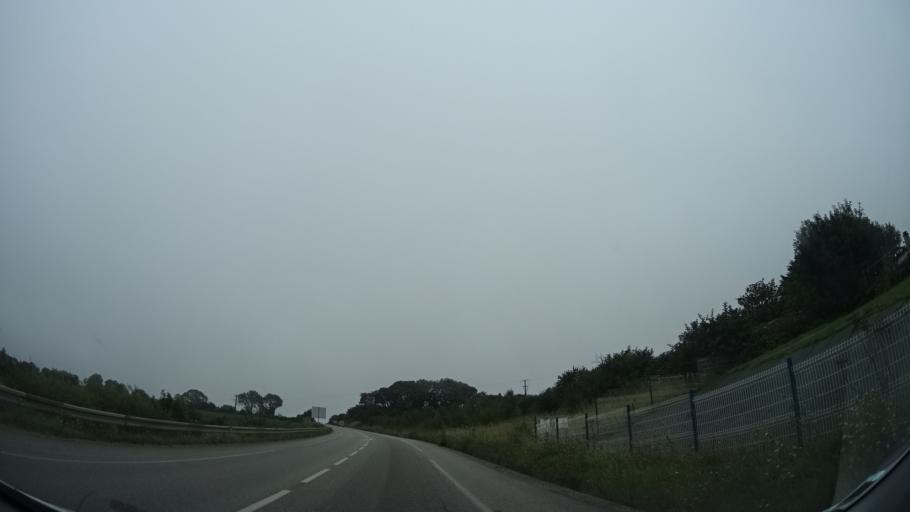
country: FR
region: Lower Normandy
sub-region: Departement de la Manche
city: Les Pieux
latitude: 49.5177
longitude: -1.8108
